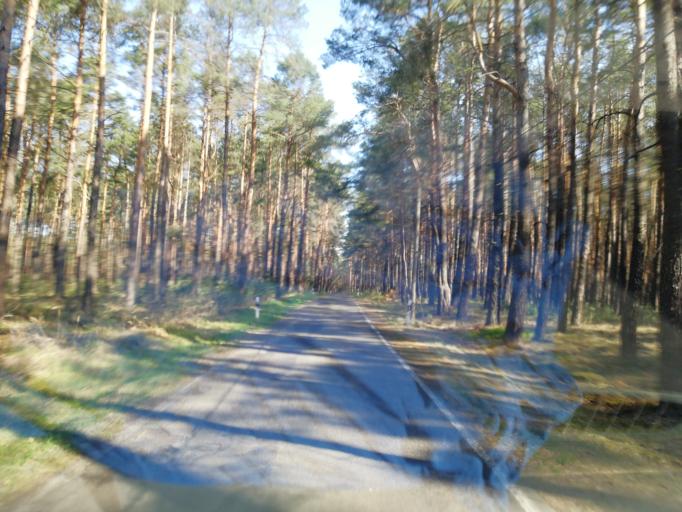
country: DE
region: Brandenburg
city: Bronkow
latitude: 51.6818
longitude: 13.8644
